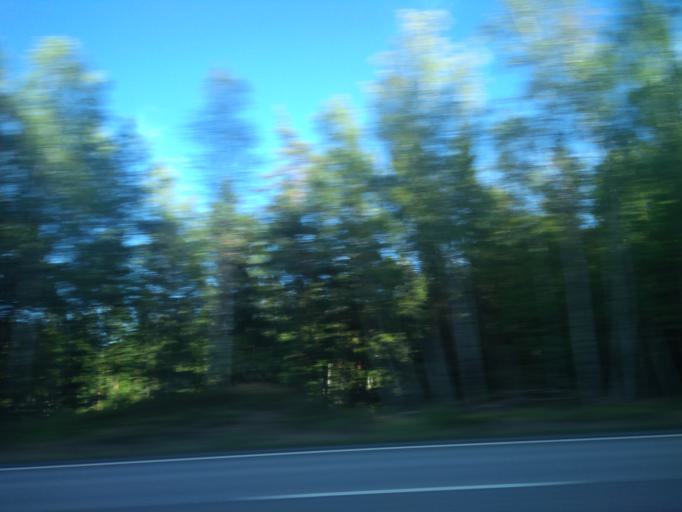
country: SE
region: OEstergoetland
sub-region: Norrkopings Kommun
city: Jursla
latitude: 58.7488
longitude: 16.1758
